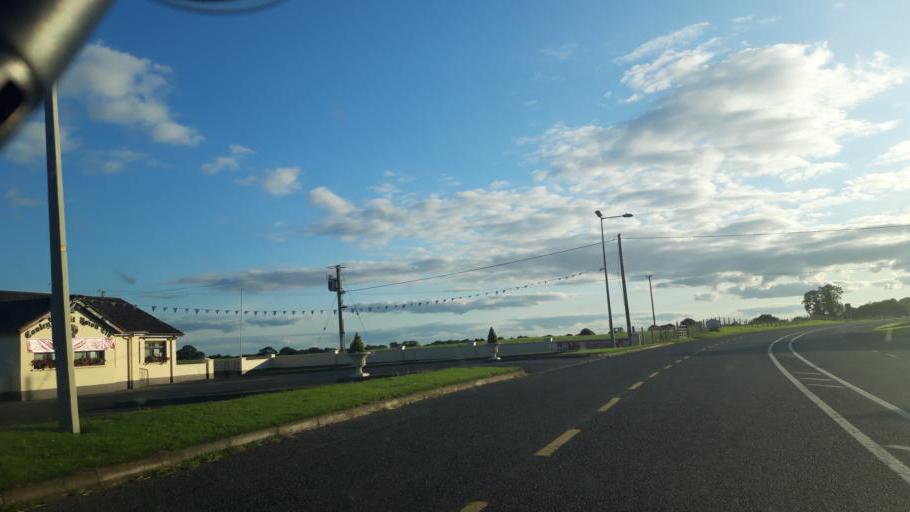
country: IE
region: Leinster
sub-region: Lu
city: Carlingford
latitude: 54.0091
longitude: -6.1683
